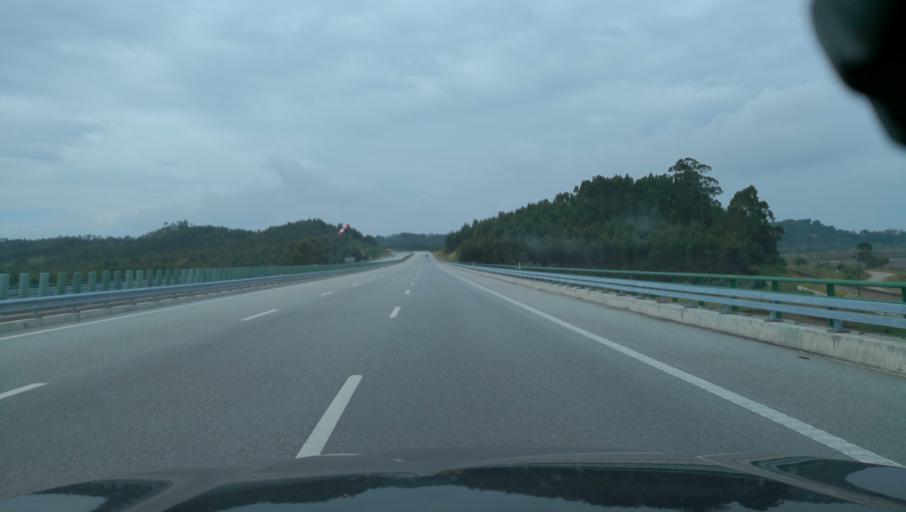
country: PT
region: Coimbra
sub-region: Figueira da Foz
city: Alhadas
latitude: 40.1283
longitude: -8.7451
